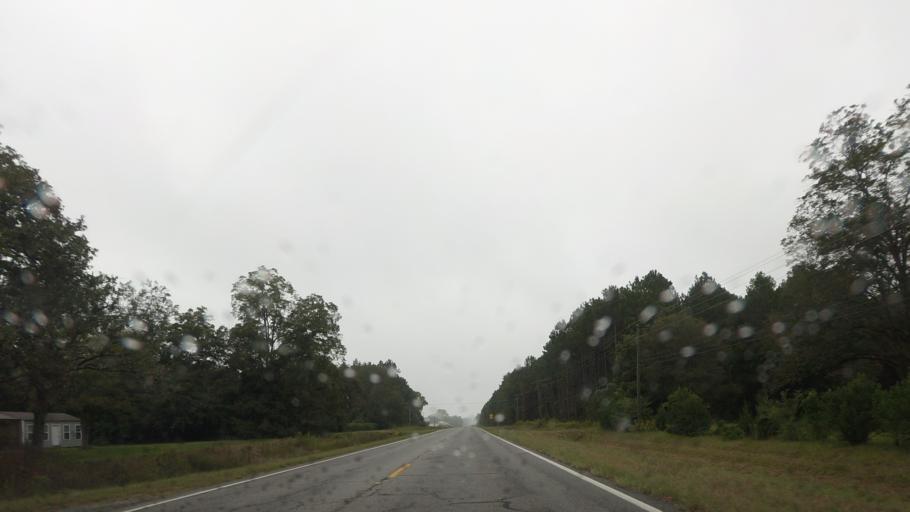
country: US
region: Georgia
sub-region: Ben Hill County
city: Fitzgerald
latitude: 31.7371
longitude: -83.2462
